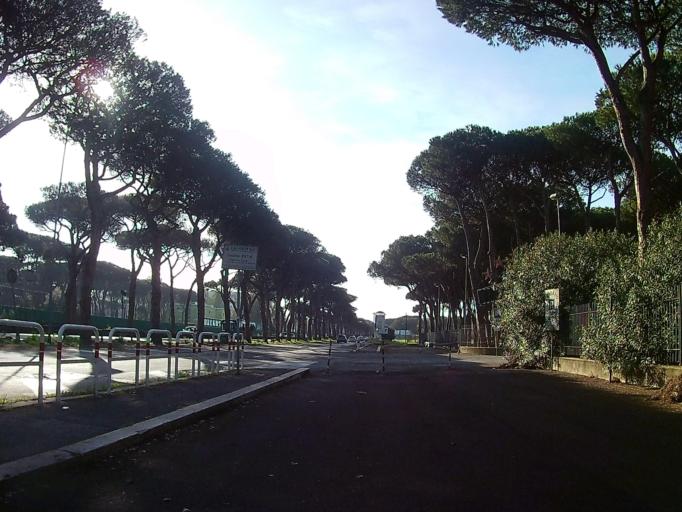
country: IT
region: Latium
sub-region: Citta metropolitana di Roma Capitale
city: Lido di Ostia
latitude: 41.7464
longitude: 12.2883
